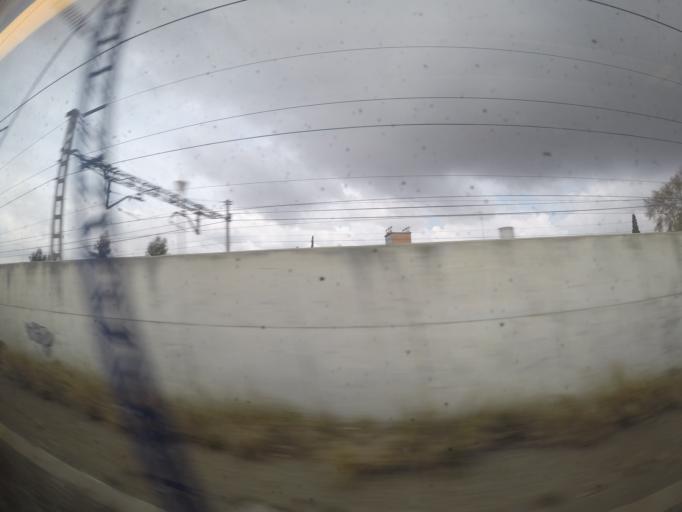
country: ES
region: Catalonia
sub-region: Provincia de Barcelona
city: Castellet
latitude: 41.2942
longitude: 1.6251
